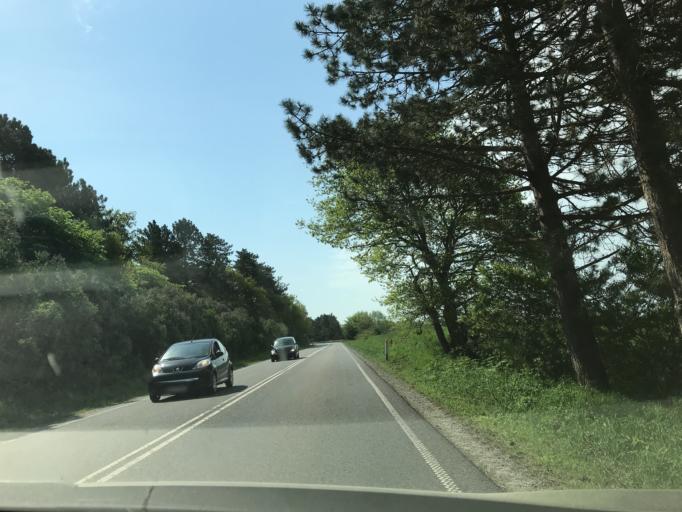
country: DK
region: South Denmark
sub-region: Middelfart Kommune
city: Ejby
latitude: 55.3635
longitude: 9.9273
